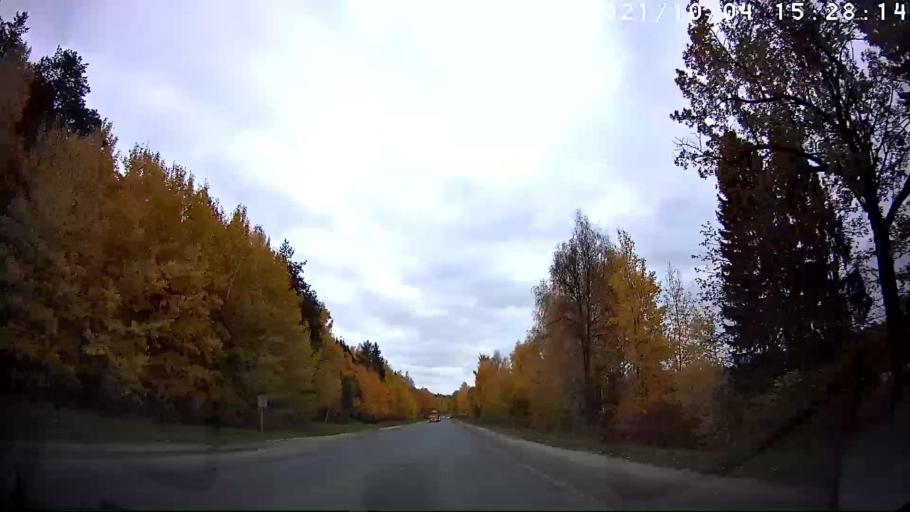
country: RU
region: Mariy-El
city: Yoshkar-Ola
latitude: 56.6118
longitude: 47.9628
